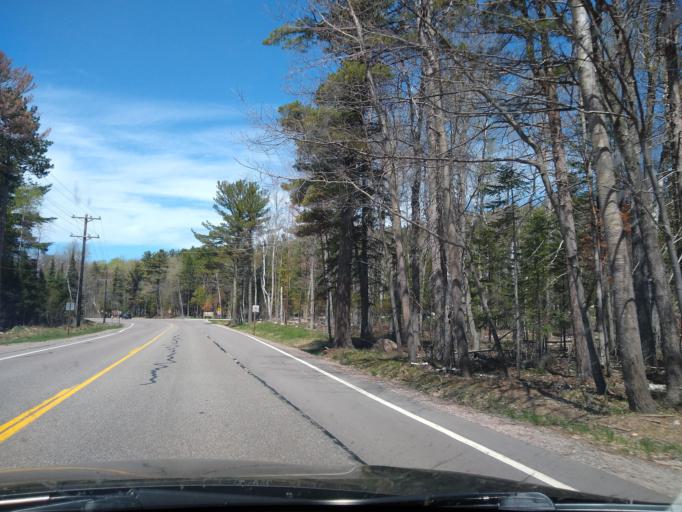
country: US
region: Michigan
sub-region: Marquette County
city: Trowbridge Park
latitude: 46.6000
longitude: -87.4574
